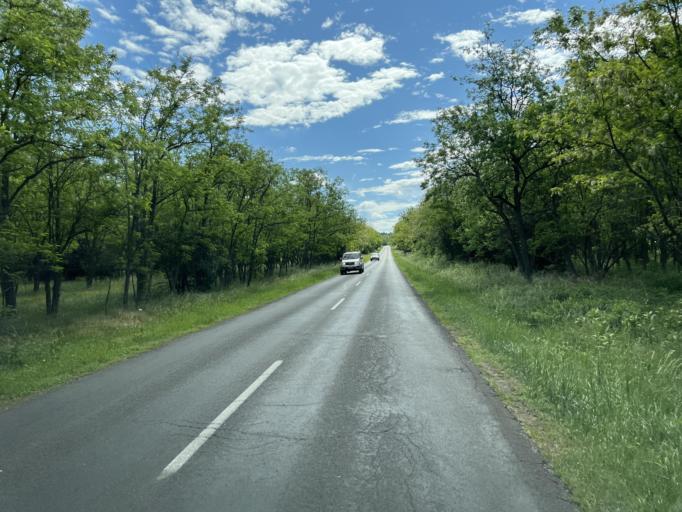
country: HU
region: Pest
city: Isaszeg
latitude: 47.5780
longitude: 19.4055
